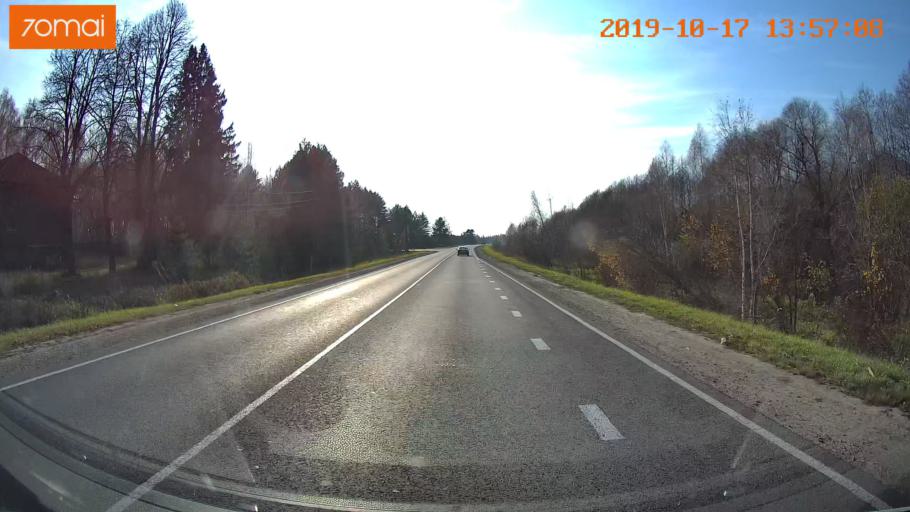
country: RU
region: Rjazan
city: Spas-Klepiki
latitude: 55.1460
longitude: 40.2520
